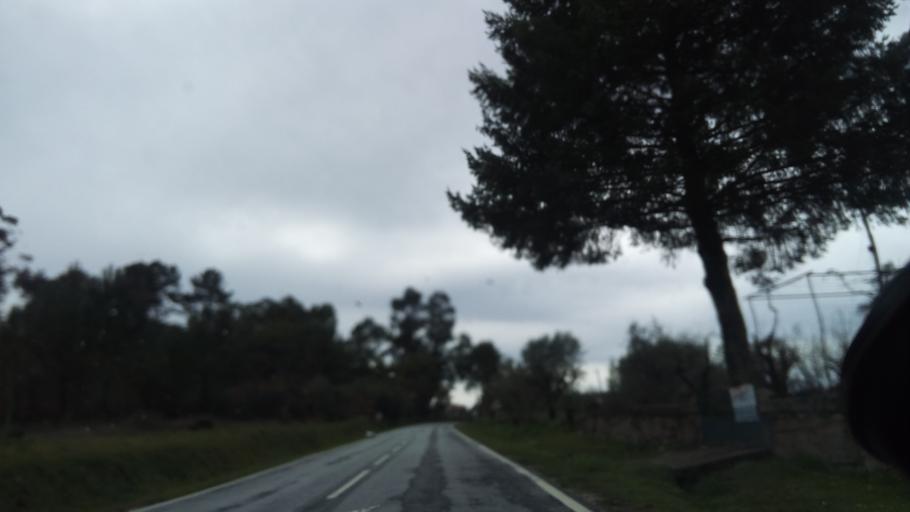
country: PT
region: Guarda
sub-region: Seia
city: Seia
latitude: 40.4815
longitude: -7.6648
